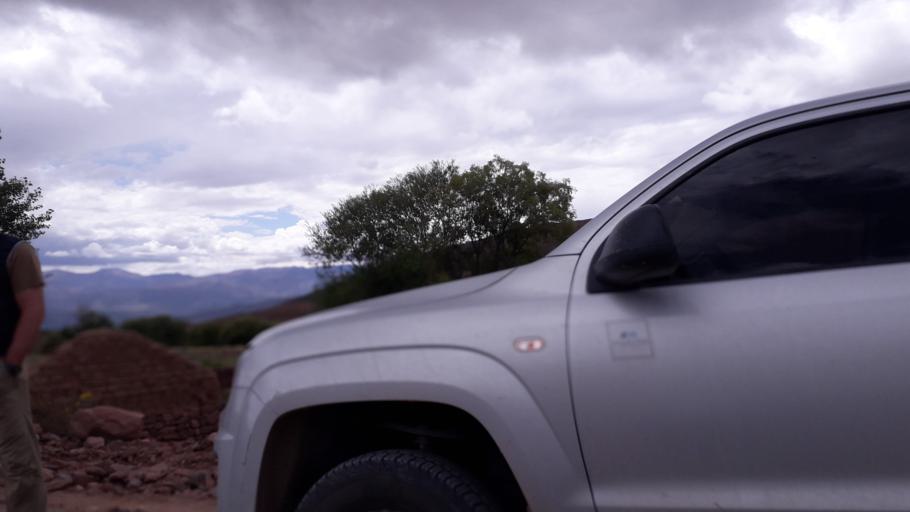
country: AR
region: Jujuy
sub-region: Departamento de Humahuaca
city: Humahuaca
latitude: -23.2029
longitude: -65.2356
